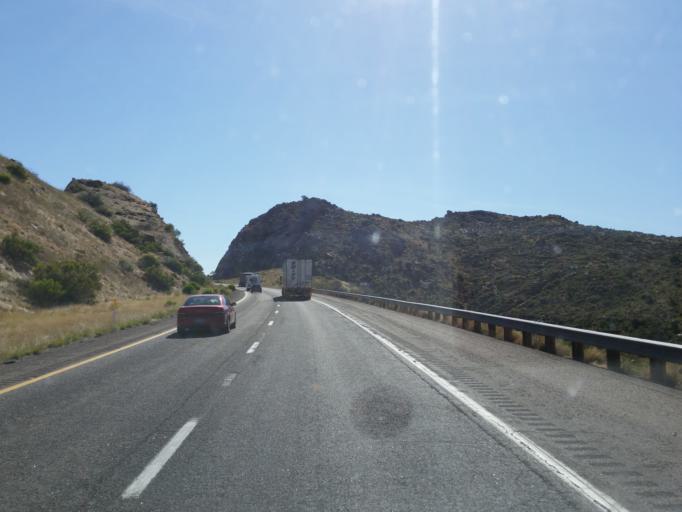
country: US
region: Arizona
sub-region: Mohave County
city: Peach Springs
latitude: 35.1705
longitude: -113.5128
